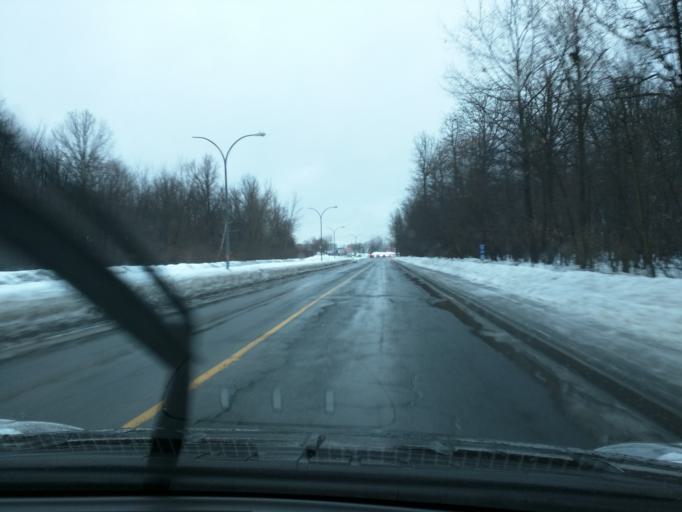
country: CA
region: Quebec
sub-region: Monteregie
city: Longueuil
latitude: 45.5479
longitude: -73.4894
